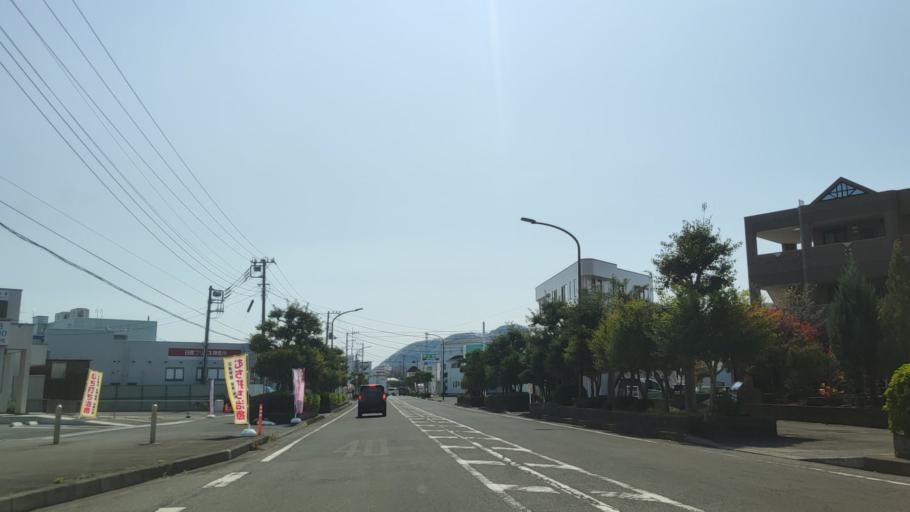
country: JP
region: Kanagawa
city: Oiso
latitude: 35.3378
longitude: 139.3048
